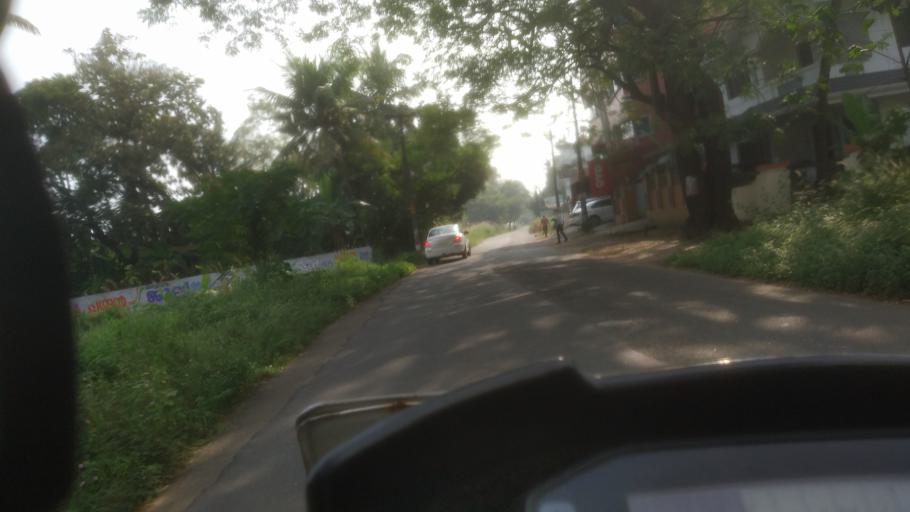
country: IN
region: Kerala
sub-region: Ernakulam
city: Angamali
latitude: 10.1624
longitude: 76.3764
